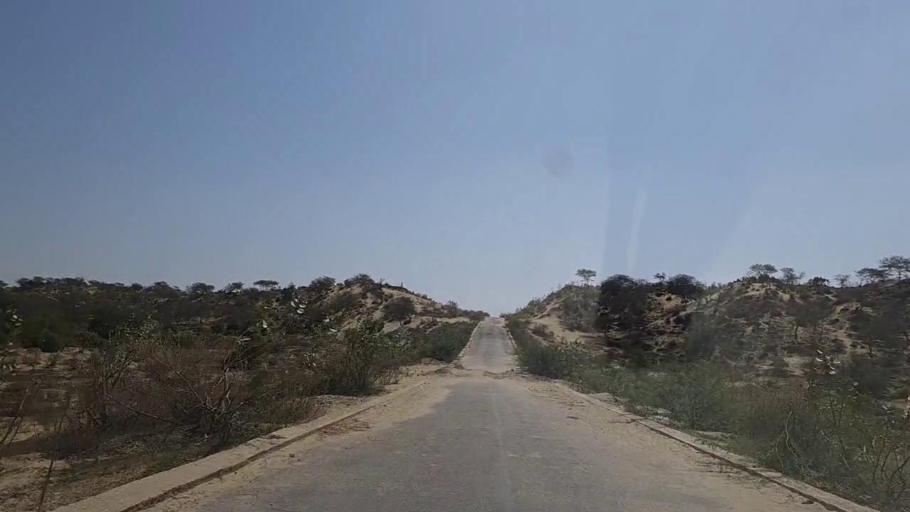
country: PK
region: Sindh
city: Diplo
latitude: 24.5073
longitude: 69.4237
